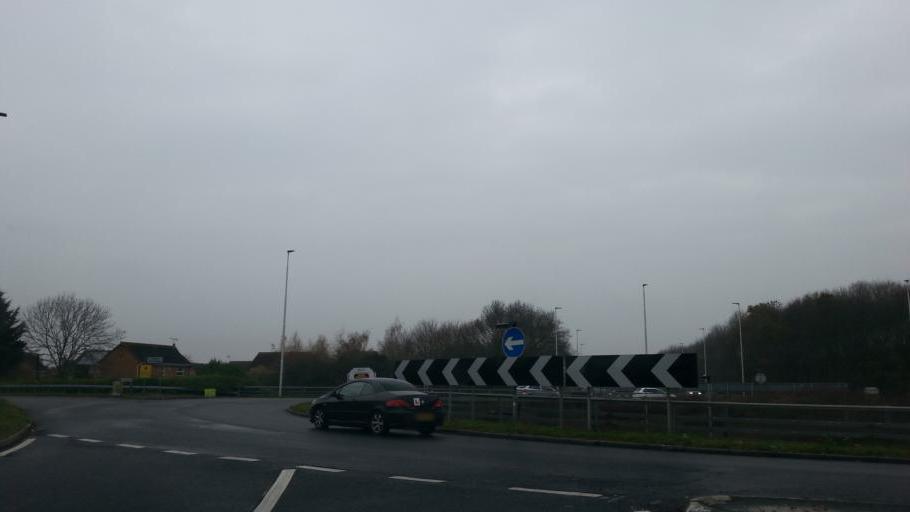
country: GB
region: England
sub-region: Peterborough
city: Castor
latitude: 52.5445
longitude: -0.3070
